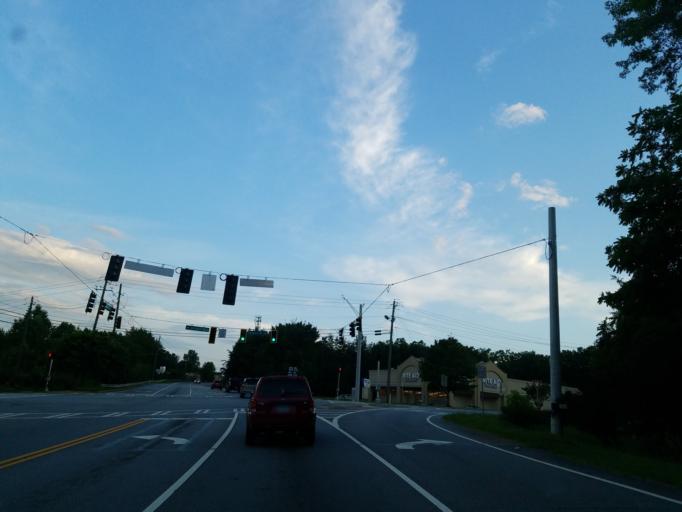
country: US
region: Georgia
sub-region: Lumpkin County
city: Dahlonega
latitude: 34.5375
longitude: -83.9760
